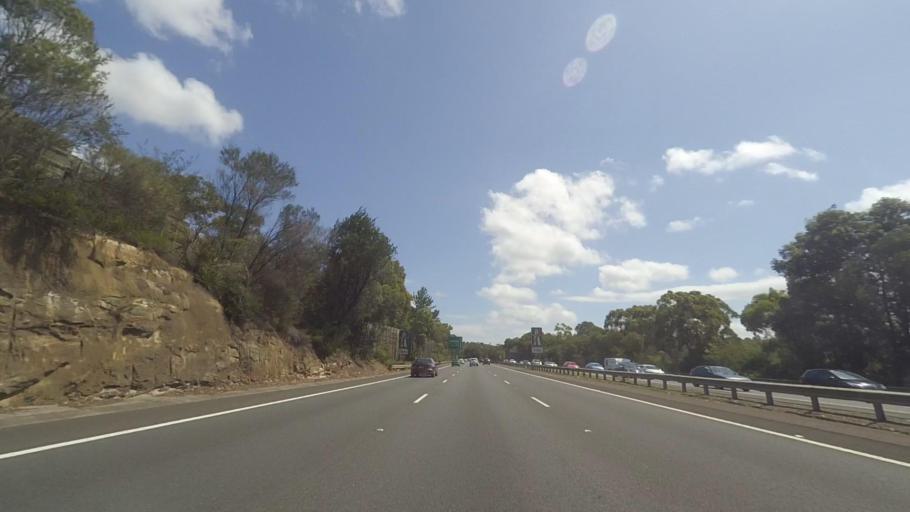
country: AU
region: New South Wales
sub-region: Ku-ring-gai
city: North Wahroonga
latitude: -33.6962
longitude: 151.1205
